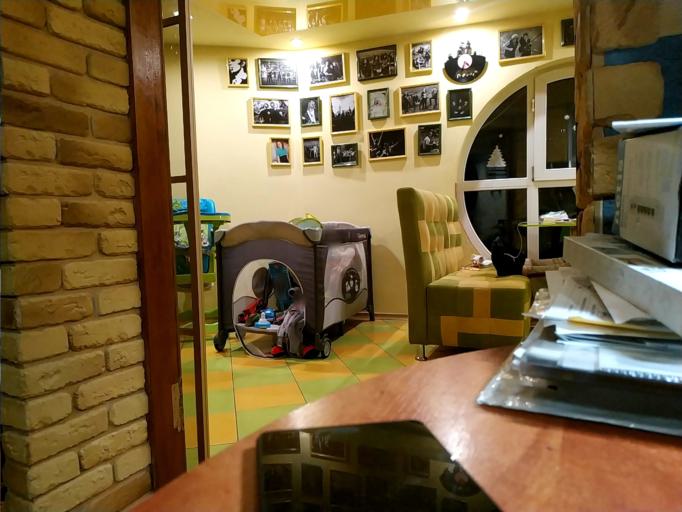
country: RU
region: Orjol
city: Naryshkino
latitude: 53.0679
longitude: 35.6715
